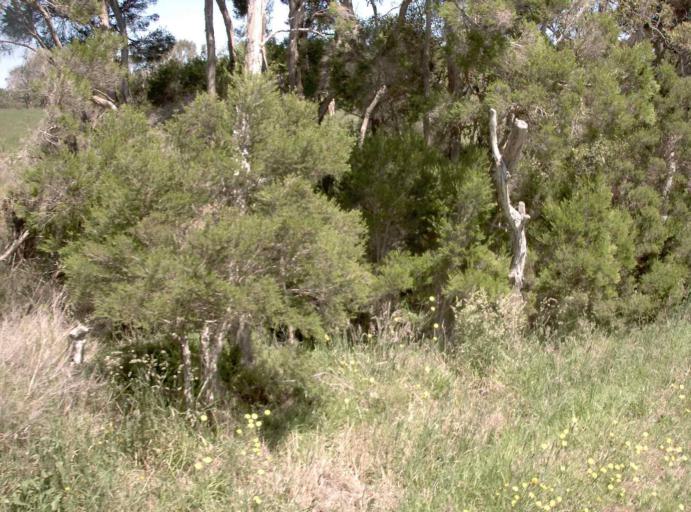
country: AU
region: Victoria
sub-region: Bass Coast
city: North Wonthaggi
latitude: -38.7533
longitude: 146.0743
